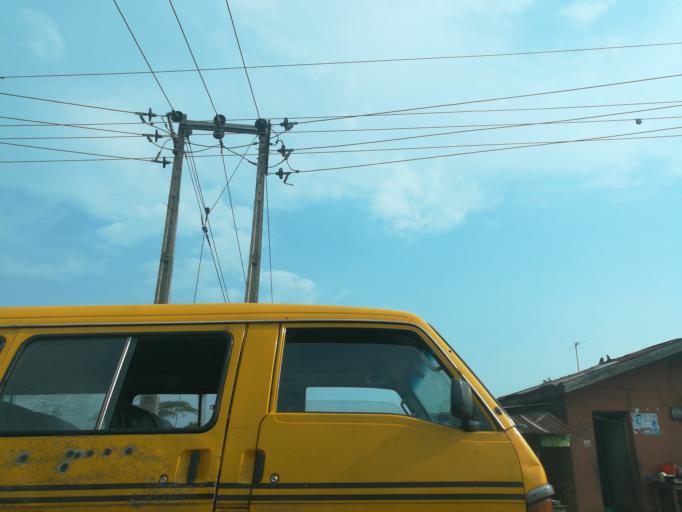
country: NG
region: Lagos
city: Ikorodu
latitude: 6.6626
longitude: 3.6725
